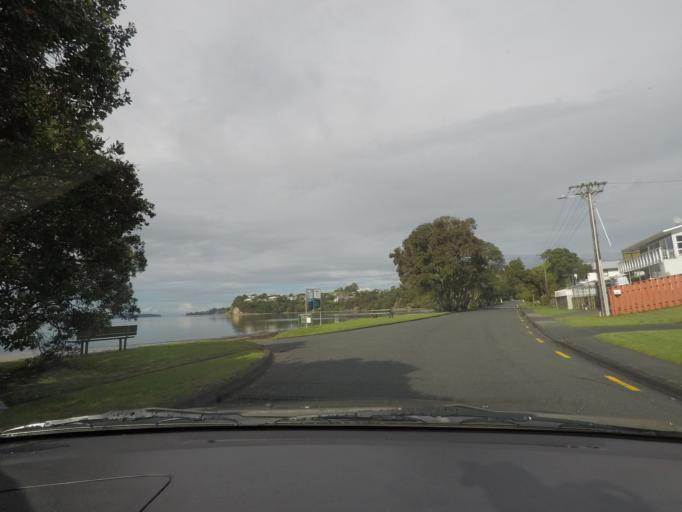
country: NZ
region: Auckland
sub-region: Auckland
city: Warkworth
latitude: -36.4213
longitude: 174.7304
